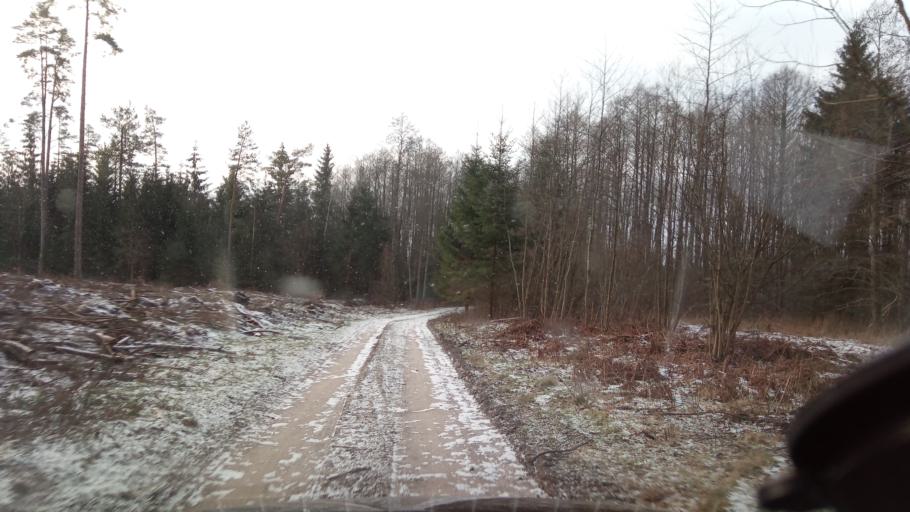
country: LT
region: Alytaus apskritis
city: Varena
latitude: 54.1270
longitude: 24.6771
